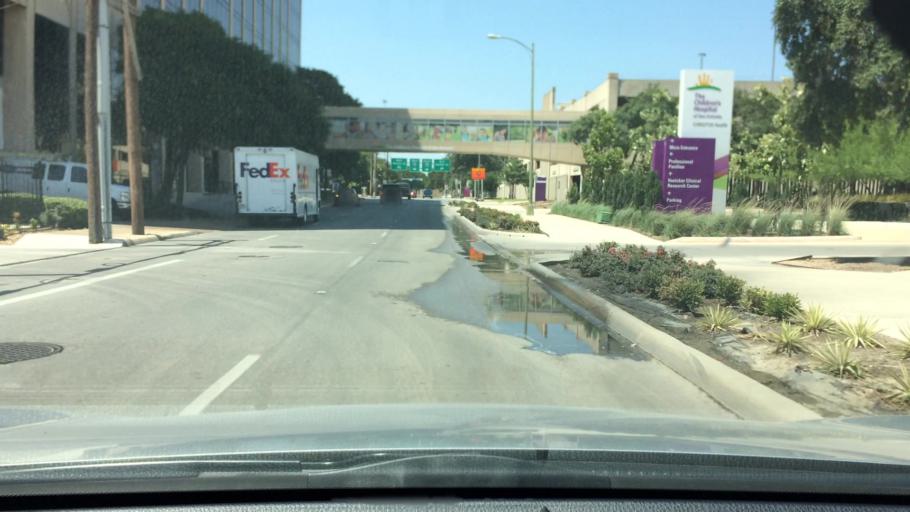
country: US
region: Texas
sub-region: Bexar County
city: San Antonio
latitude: 29.4273
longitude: -98.5000
